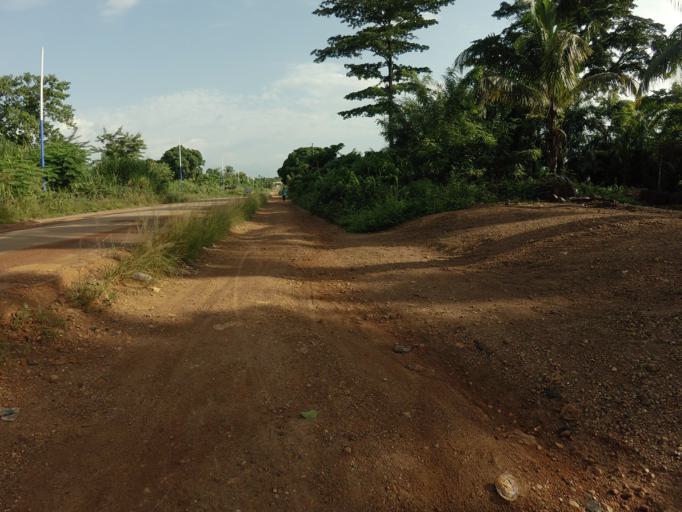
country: GH
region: Volta
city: Hohoe
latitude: 7.1211
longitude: 0.4582
